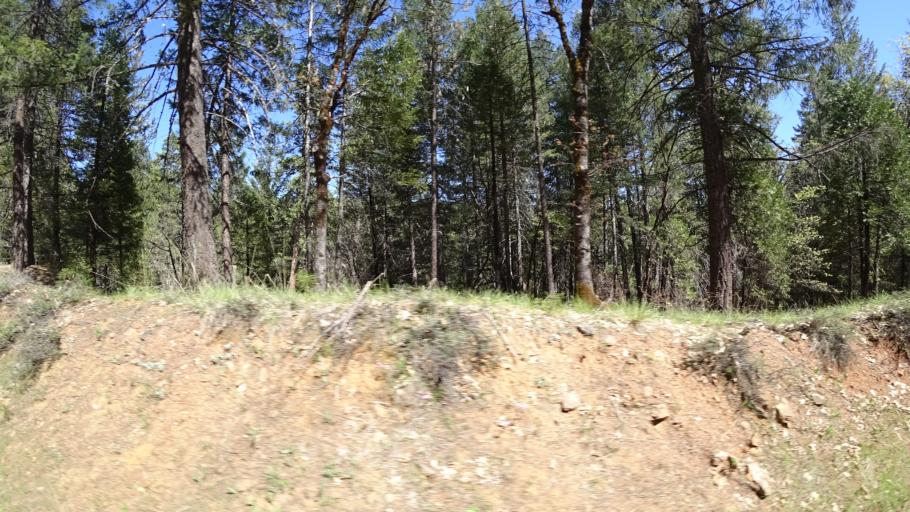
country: US
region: California
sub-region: Trinity County
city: Lewiston
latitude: 40.8780
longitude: -122.8030
